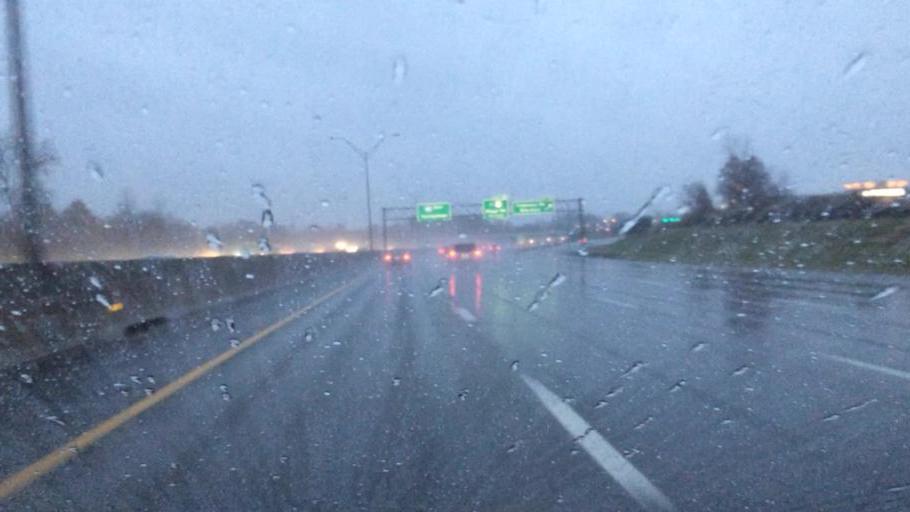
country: US
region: Ohio
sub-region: Cuyahoga County
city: Brooklyn
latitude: 41.4252
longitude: -81.7673
